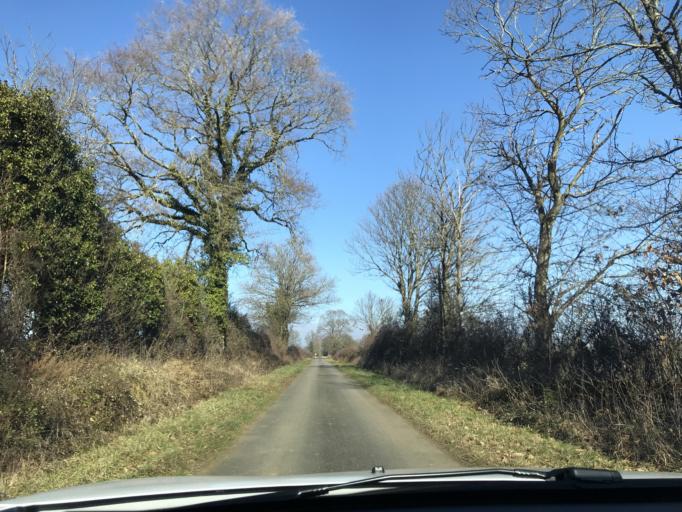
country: FR
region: Poitou-Charentes
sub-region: Departement de la Charente
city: Saint-Claud
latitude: 45.8571
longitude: 0.5307
